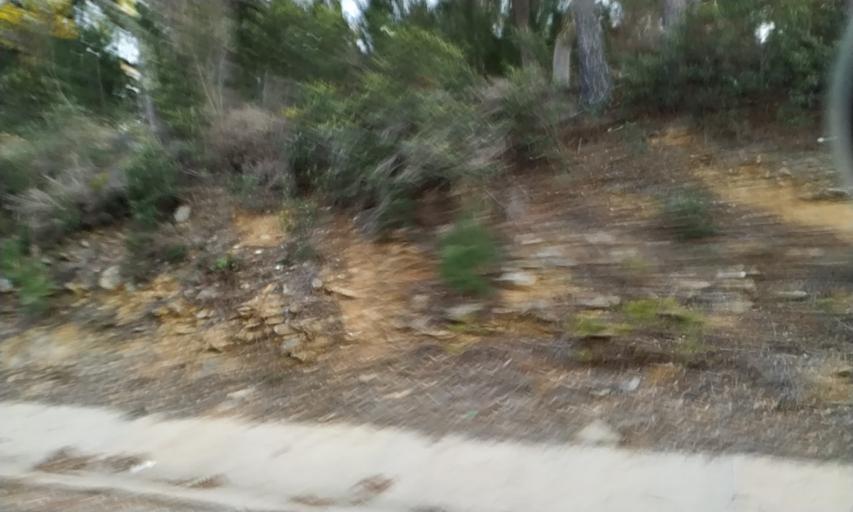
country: PT
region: Portalegre
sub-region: Portalegre
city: Sao Juliao
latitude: 39.3431
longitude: -7.2935
